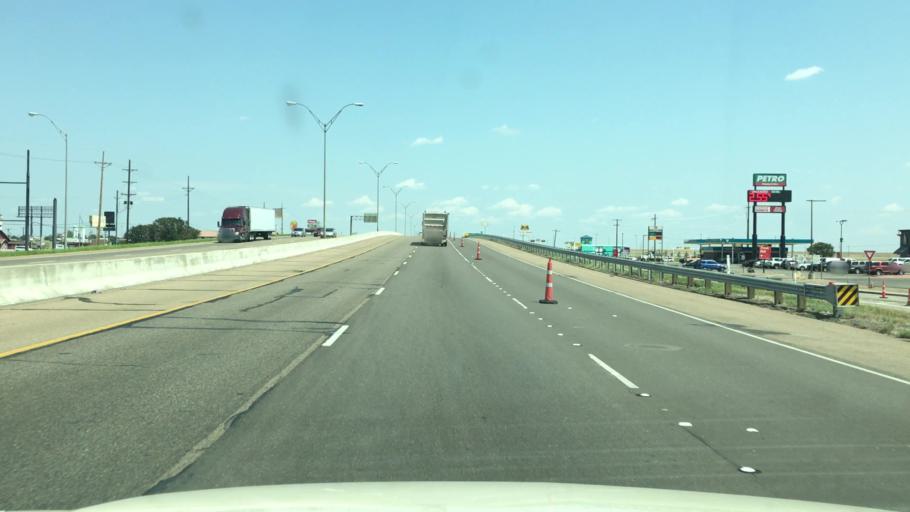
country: US
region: Texas
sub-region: Potter County
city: Amarillo
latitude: 35.1926
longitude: -101.7452
